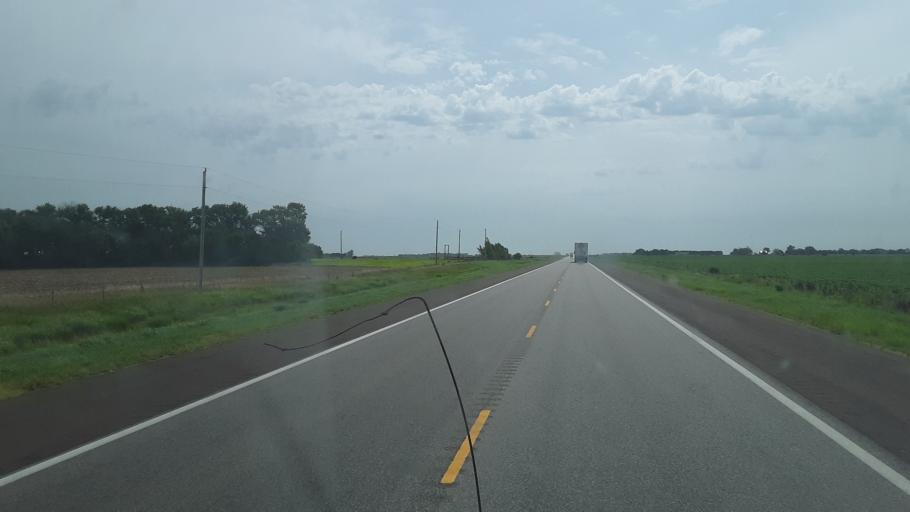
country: US
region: Kansas
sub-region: Reno County
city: Nickerson
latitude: 37.9849
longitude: -98.1233
